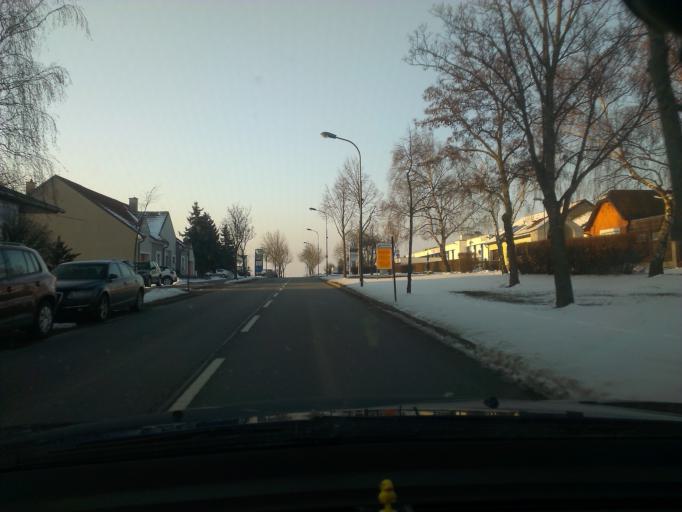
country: AT
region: Burgenland
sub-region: Eisenstadt-Umgebung
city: Breitenbrunn
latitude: 47.9405
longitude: 16.7285
